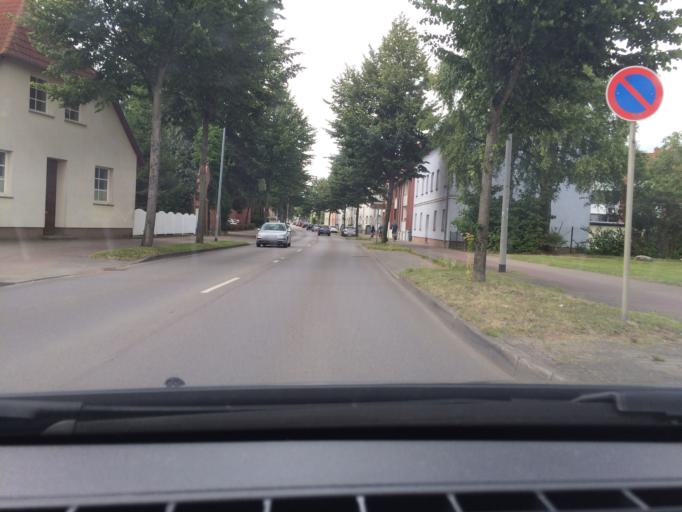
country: DE
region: Mecklenburg-Vorpommern
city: Stralsund
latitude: 54.3248
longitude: 13.0771
